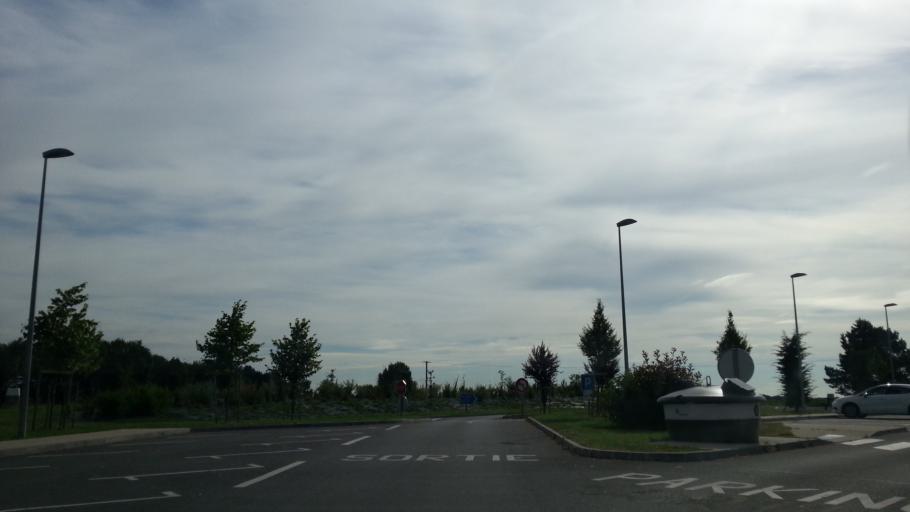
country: FR
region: Picardie
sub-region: Departement de l'Aisne
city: Fere-en-Tardenois
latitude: 49.1258
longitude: 3.5378
